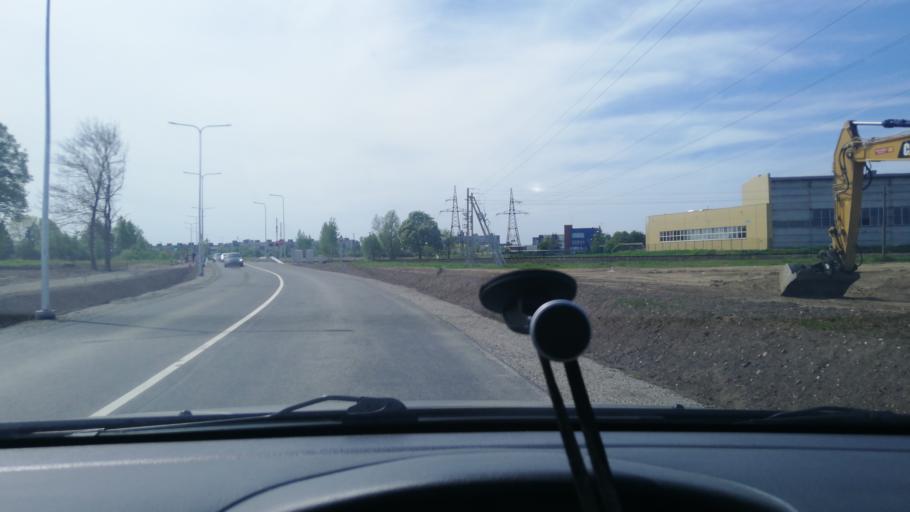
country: LT
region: Klaipedos apskritis
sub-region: Klaipeda
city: Klaipeda
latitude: 55.6842
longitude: 21.1981
